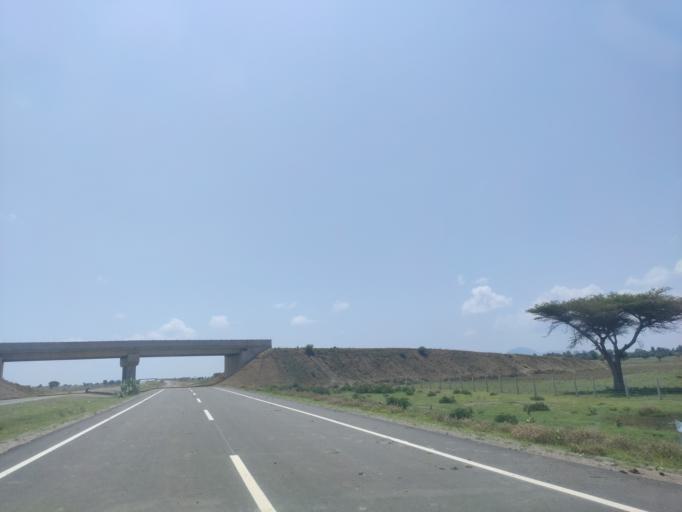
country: ET
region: Oromiya
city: Ziway
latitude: 8.2324
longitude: 38.8747
